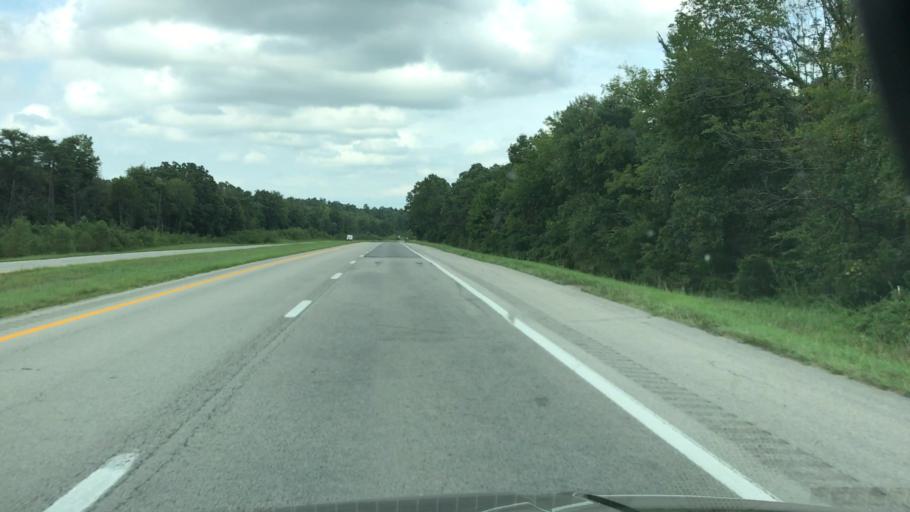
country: US
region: Kentucky
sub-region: Caldwell County
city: Princeton
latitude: 37.1484
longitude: -87.7976
